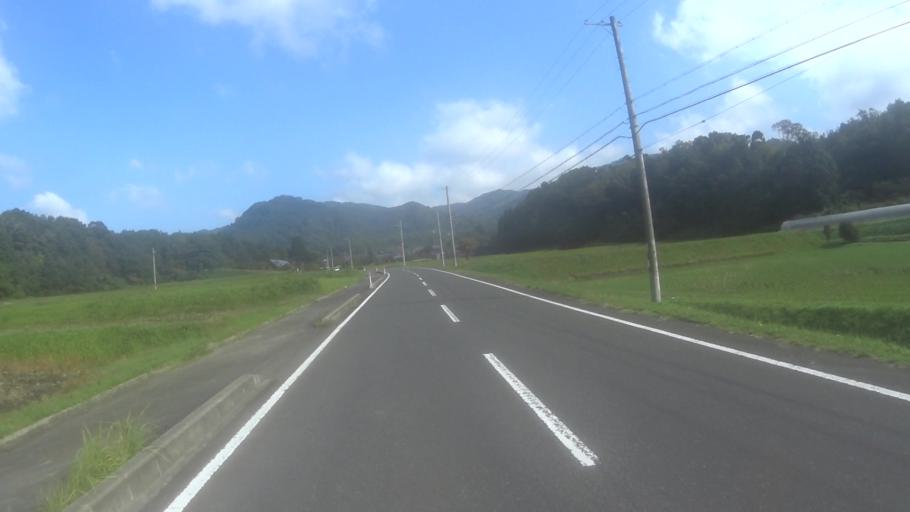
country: JP
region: Kyoto
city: Miyazu
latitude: 35.6037
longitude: 135.1471
